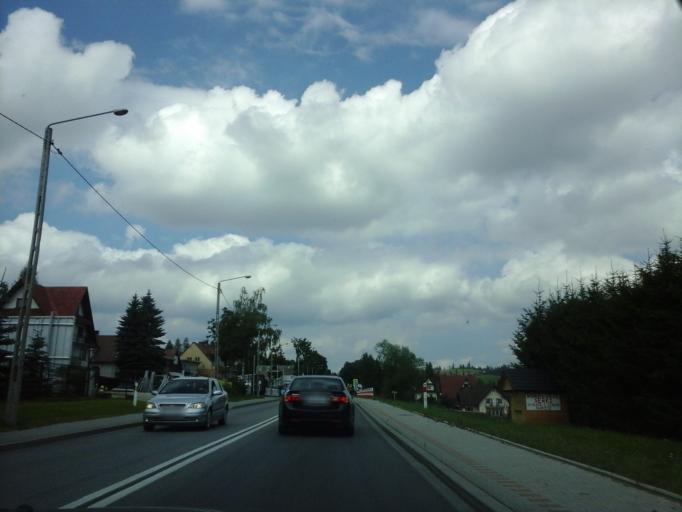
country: PL
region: Lesser Poland Voivodeship
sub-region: Powiat nowotarski
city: Lasek
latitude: 49.4967
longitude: 20.0041
